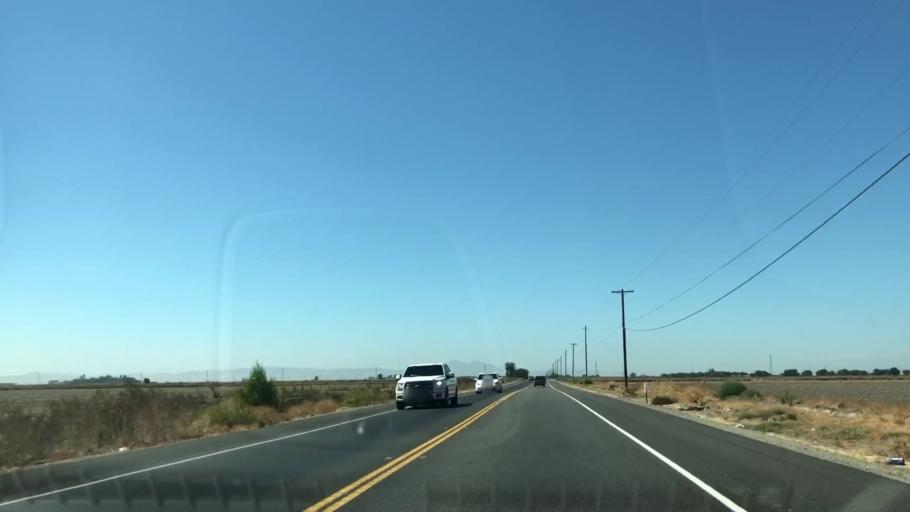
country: US
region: California
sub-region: San Joaquin County
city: Country Club
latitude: 37.9268
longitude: -121.3779
